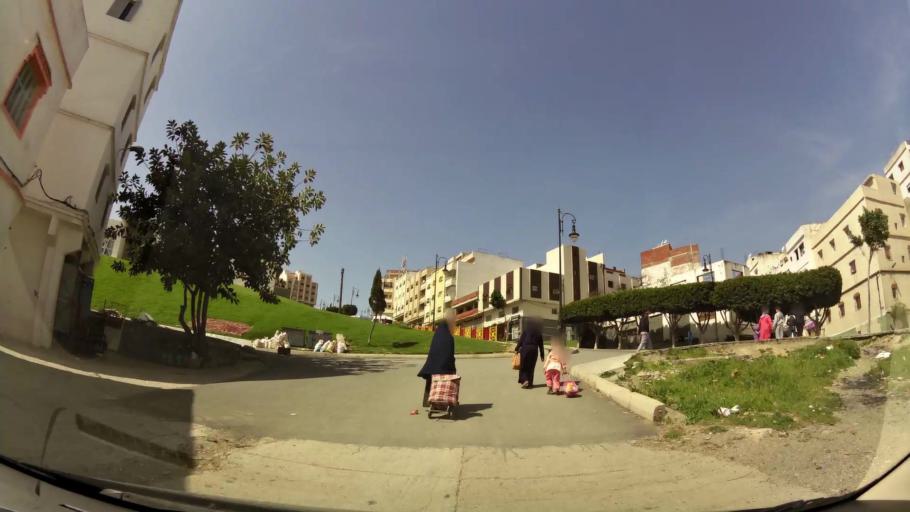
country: MA
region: Tanger-Tetouan
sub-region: Tanger-Assilah
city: Tangier
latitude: 35.7414
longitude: -5.8095
